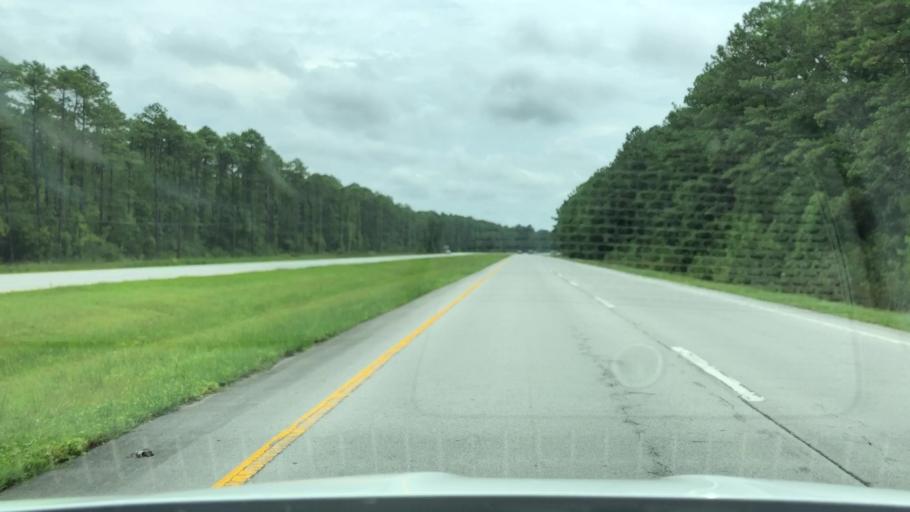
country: US
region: North Carolina
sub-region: Craven County
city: Havelock
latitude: 34.8492
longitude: -76.8869
